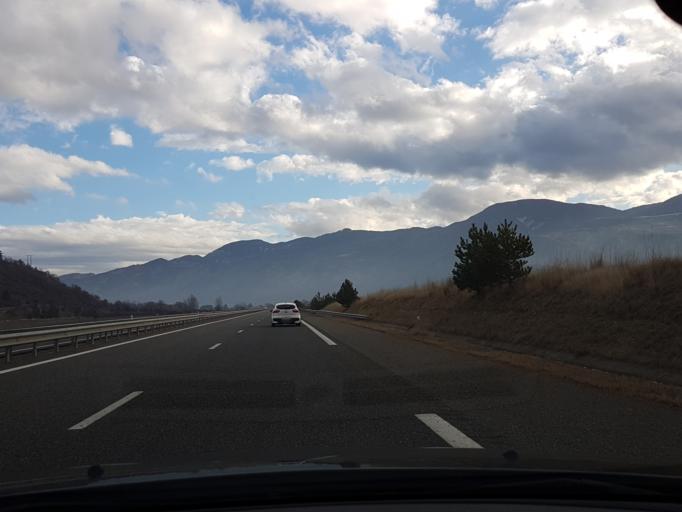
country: FR
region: Provence-Alpes-Cote d'Azur
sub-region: Departement des Hautes-Alpes
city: Tallard
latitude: 44.4182
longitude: 5.9811
